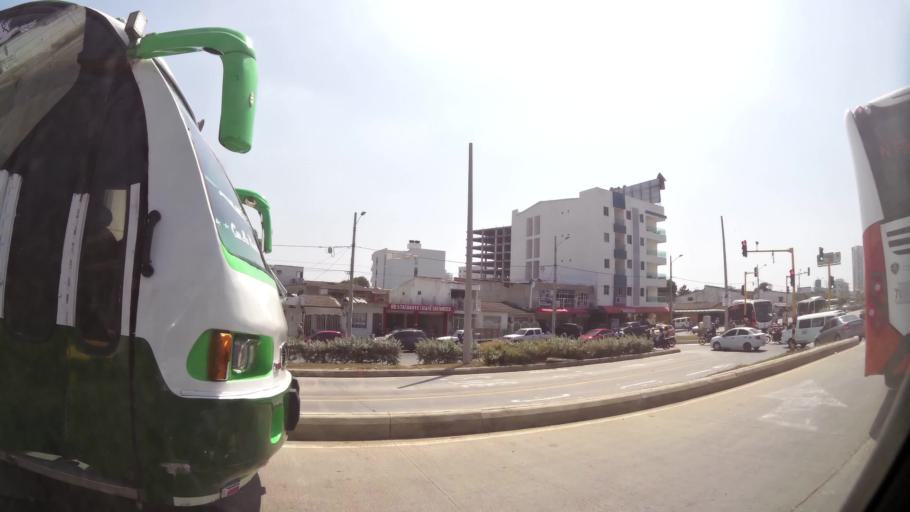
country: CO
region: Bolivar
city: Cartagena
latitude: 10.3968
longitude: -75.4750
